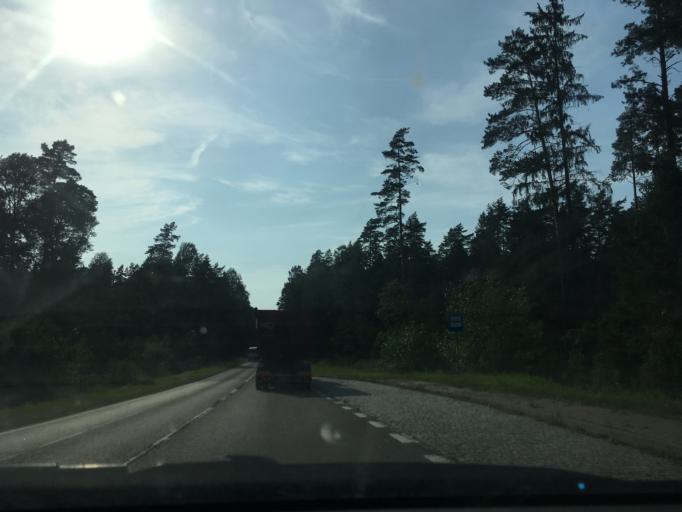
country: PL
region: Podlasie
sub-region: Powiat bialostocki
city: Suprasl
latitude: 53.1257
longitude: 23.4153
